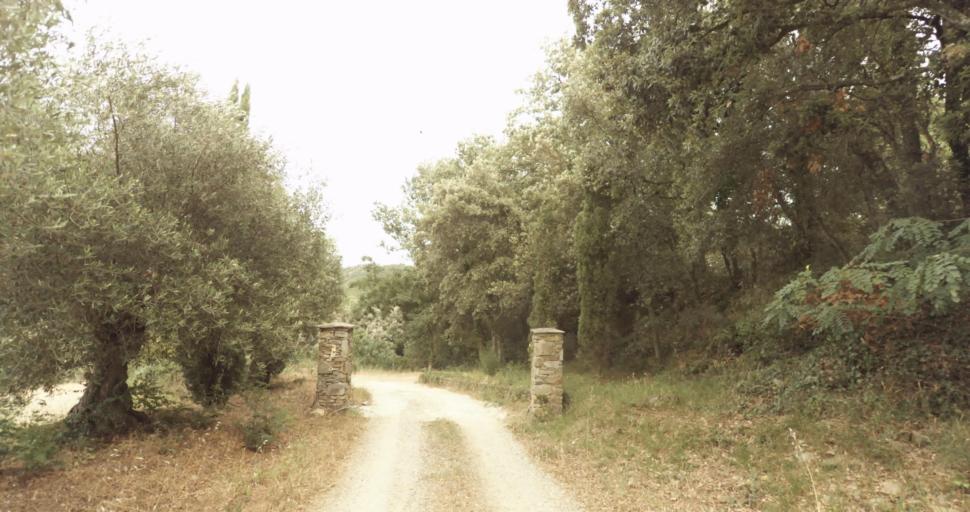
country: FR
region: Provence-Alpes-Cote d'Azur
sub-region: Departement du Var
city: La Croix-Valmer
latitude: 43.2185
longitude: 6.5732
